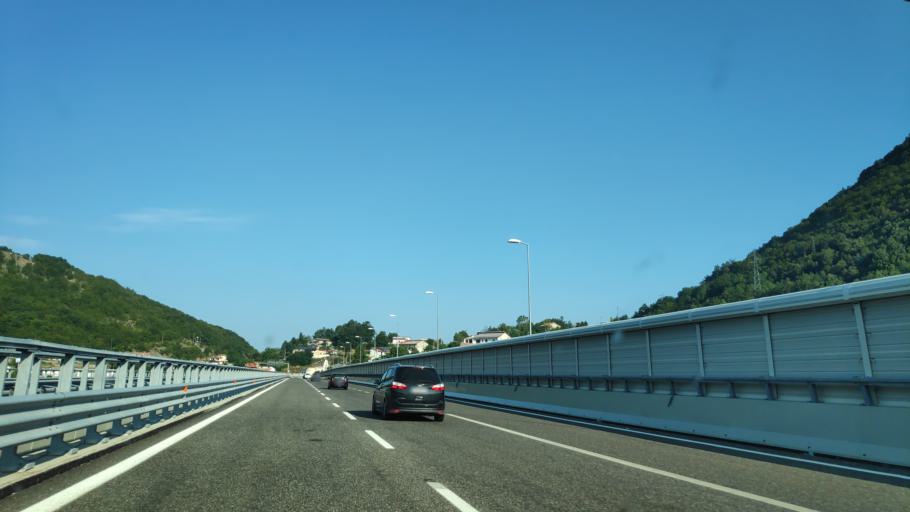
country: IT
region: Basilicate
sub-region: Provincia di Potenza
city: Lauria
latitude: 40.0188
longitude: 15.8861
